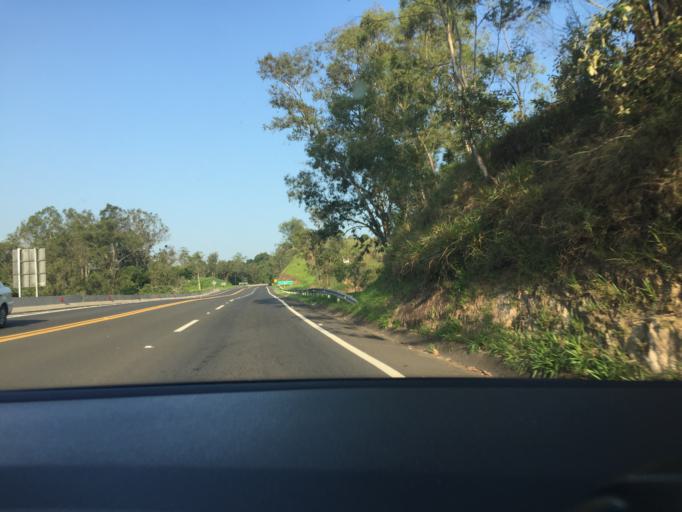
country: BR
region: Sao Paulo
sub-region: Louveira
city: Louveira
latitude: -23.0823
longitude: -46.9217
